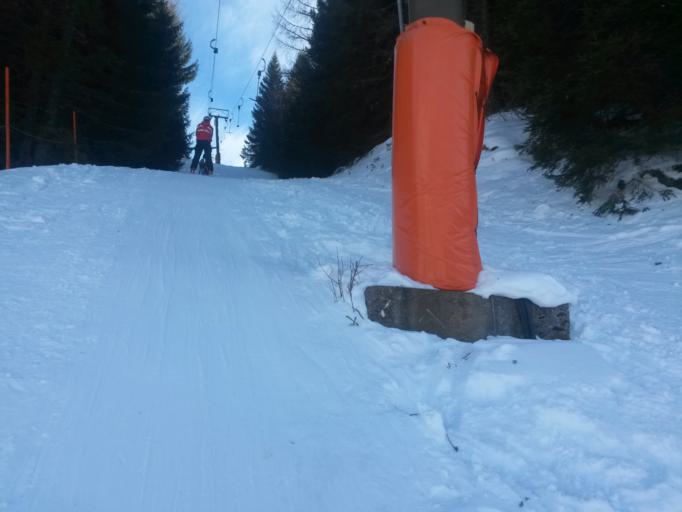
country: AT
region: Salzburg
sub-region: Politischer Bezirk Sankt Johann im Pongau
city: Dorfgastein
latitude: 47.2406
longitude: 13.1245
